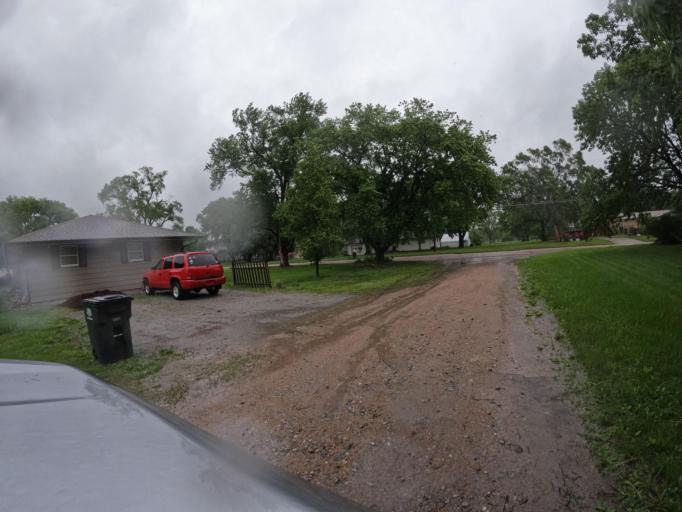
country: US
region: Nebraska
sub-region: Gage County
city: Wymore
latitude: 40.1368
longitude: -96.6625
